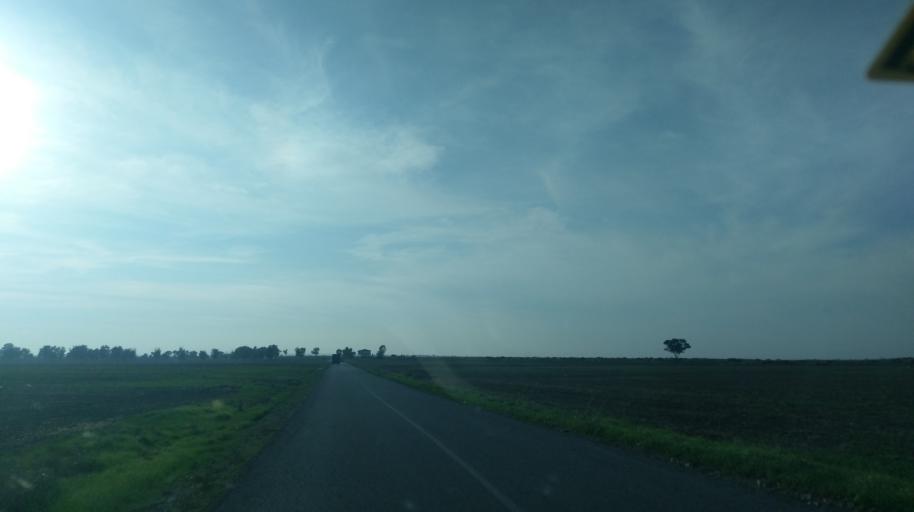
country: CY
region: Ammochostos
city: Acheritou
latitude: 35.0986
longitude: 33.8537
